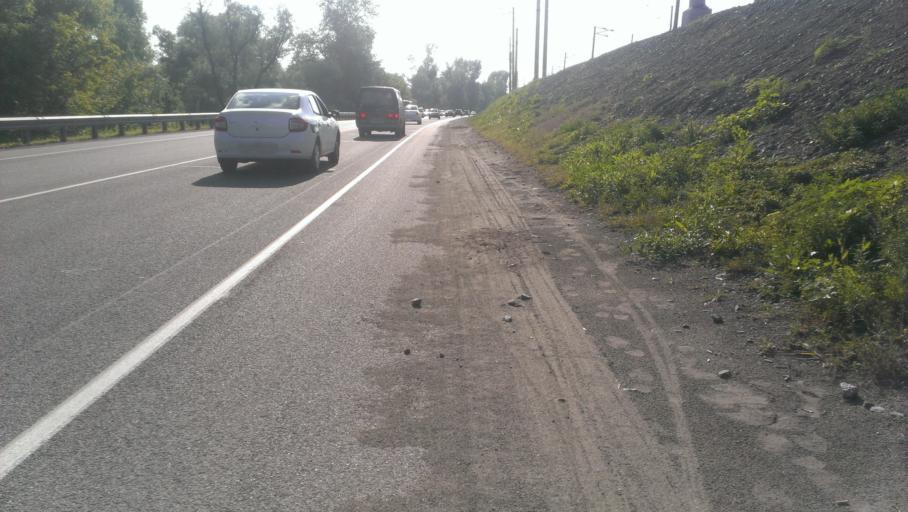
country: RU
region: Altai Krai
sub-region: Gorod Barnaulskiy
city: Barnaul
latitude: 53.3671
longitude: 83.8451
